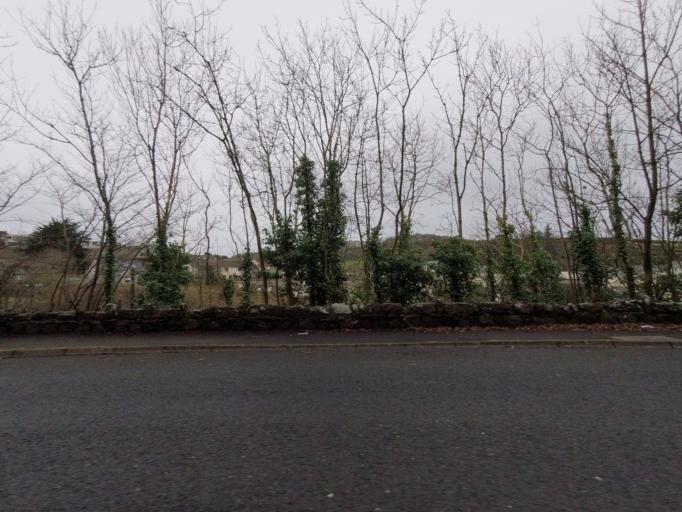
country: IE
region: Munster
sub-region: Waterford
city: Dunmore East
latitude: 52.1550
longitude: -6.9968
